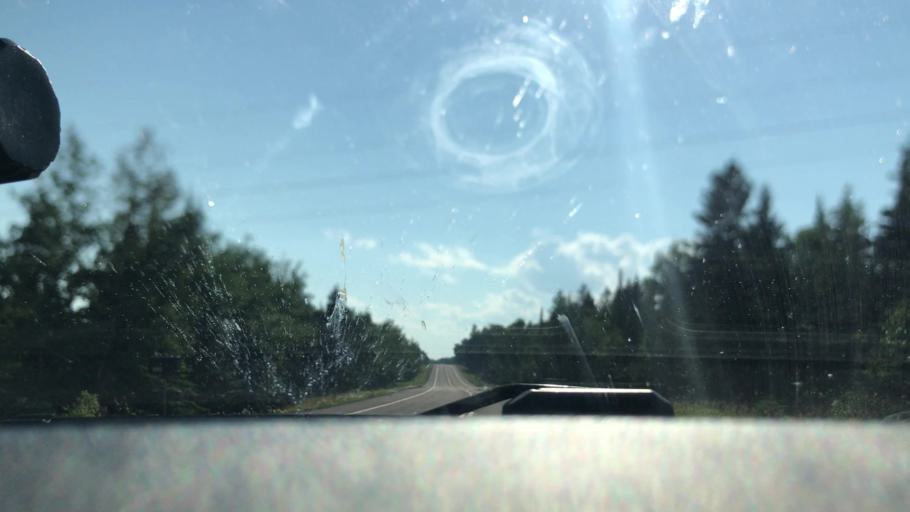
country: US
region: Minnesota
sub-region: Cook County
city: Grand Marais
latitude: 47.8290
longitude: -89.9971
